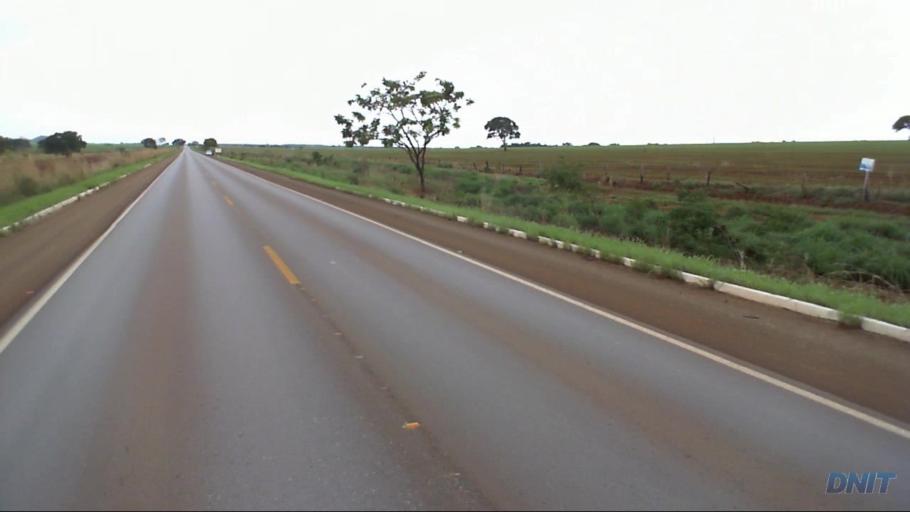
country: BR
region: Goias
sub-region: Barro Alto
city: Barro Alto
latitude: -14.8242
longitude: -49.0377
